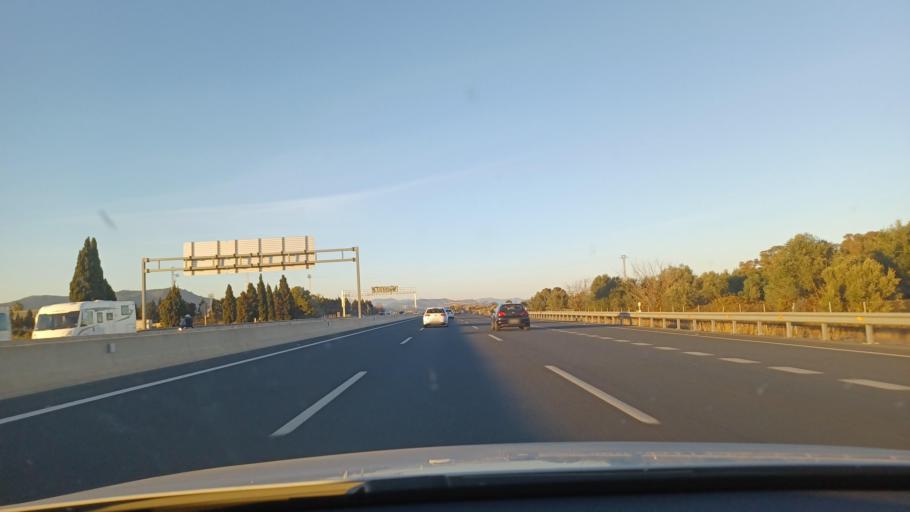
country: ES
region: Valencia
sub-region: Provincia de Valencia
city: Puig
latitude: 39.5893
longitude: -0.2934
